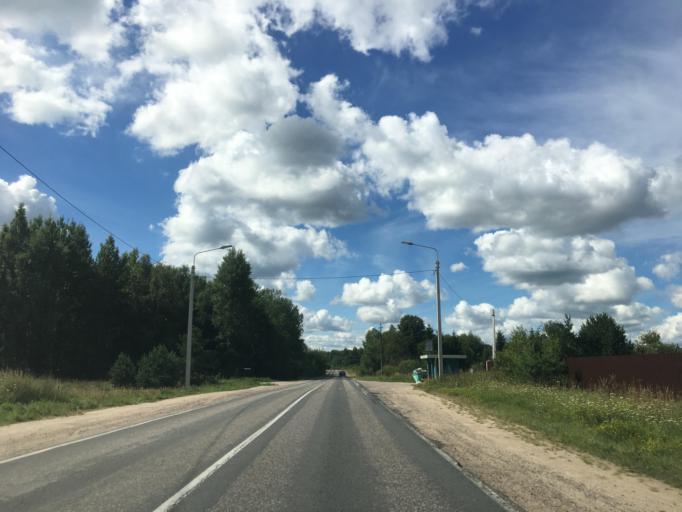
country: RU
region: Pskov
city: Pskov
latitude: 57.6915
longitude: 28.1763
